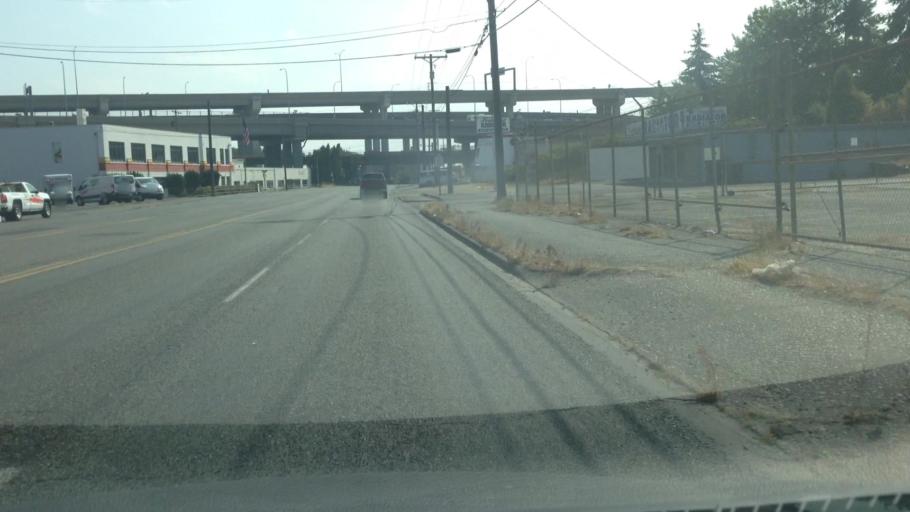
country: US
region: Washington
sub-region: Pierce County
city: Tacoma
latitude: 47.2317
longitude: -122.4662
